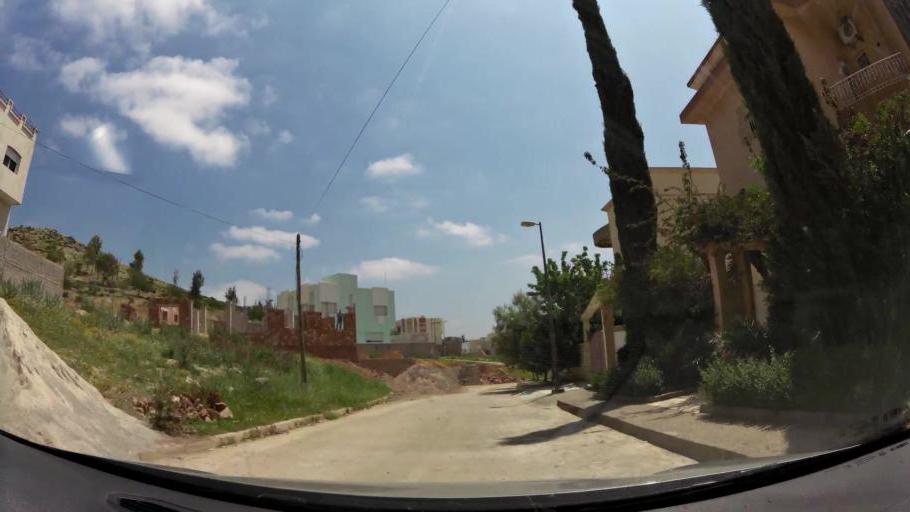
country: MA
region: Fes-Boulemane
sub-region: Fes
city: Fes
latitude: 34.0634
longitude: -5.0241
